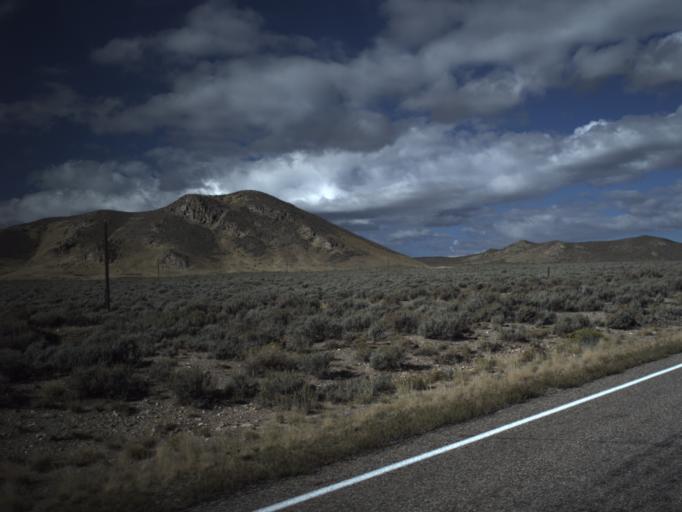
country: US
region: Utah
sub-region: Beaver County
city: Milford
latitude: 38.4185
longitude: -113.0914
